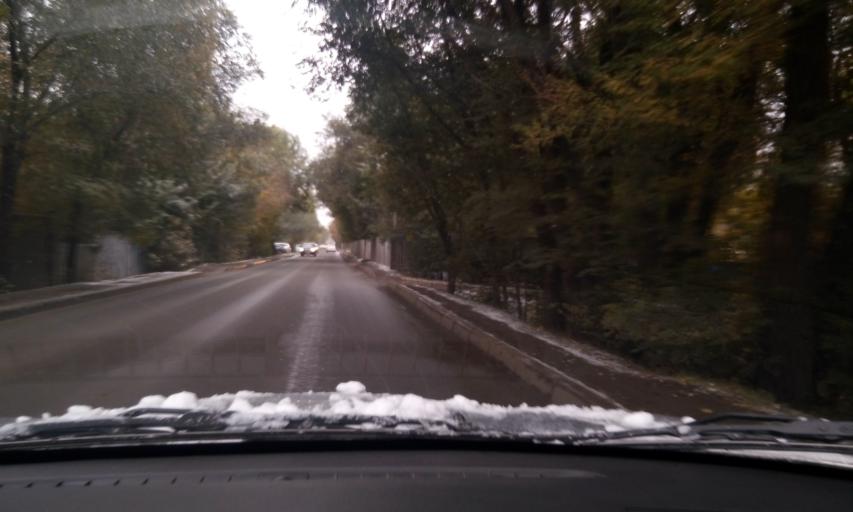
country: KZ
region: Astana Qalasy
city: Astana
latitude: 51.1399
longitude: 71.4330
